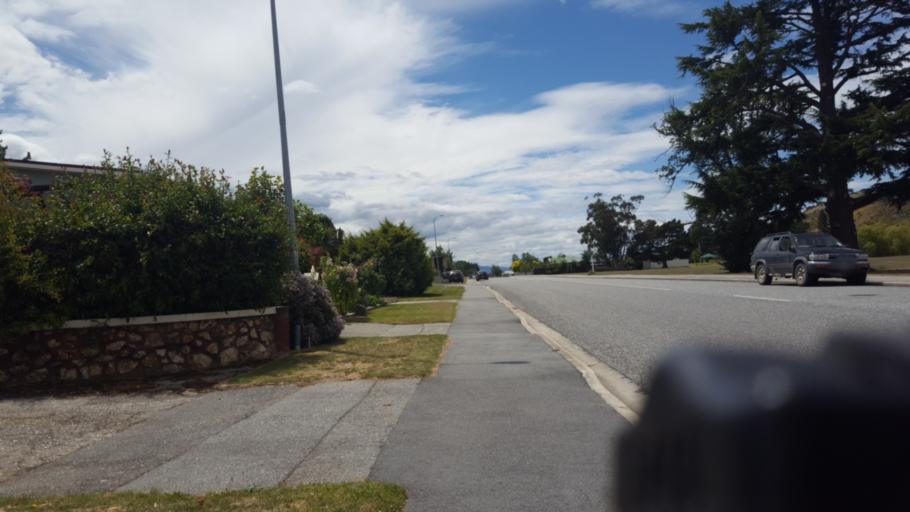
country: NZ
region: Otago
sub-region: Queenstown-Lakes District
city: Wanaka
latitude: -45.0455
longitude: 169.2127
